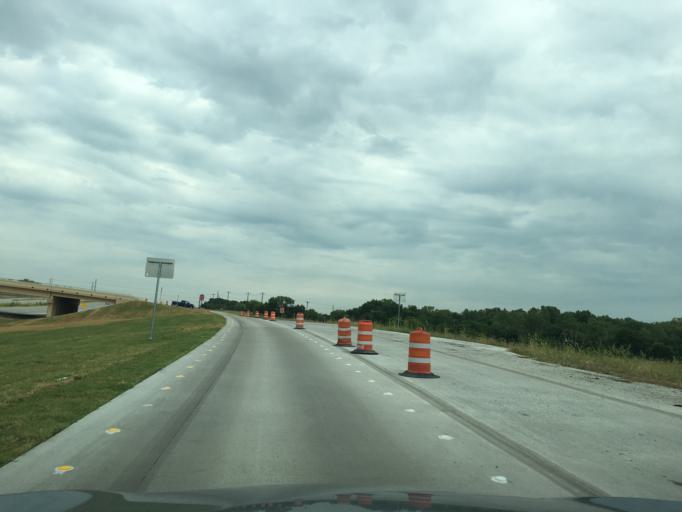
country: US
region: Texas
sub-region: Collin County
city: Melissa
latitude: 33.3079
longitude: -96.5904
